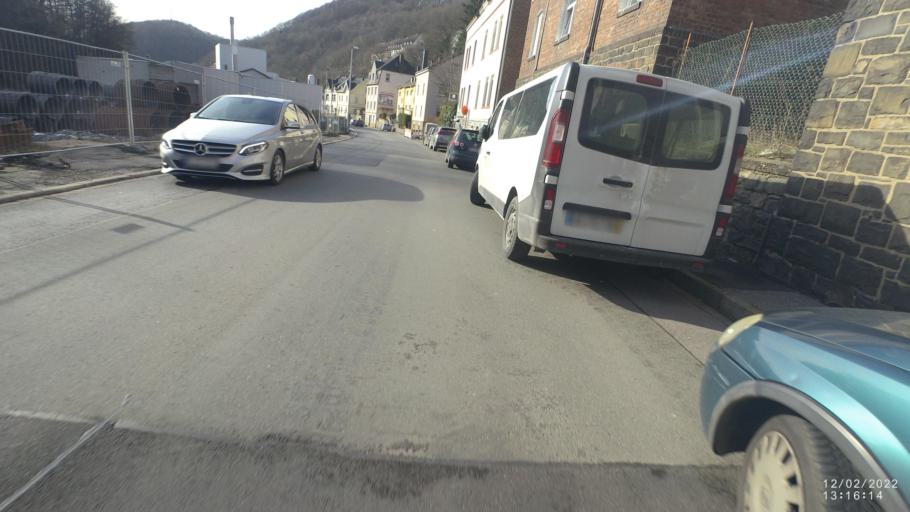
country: DE
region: North Rhine-Westphalia
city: Altena
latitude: 51.3005
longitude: 7.6907
